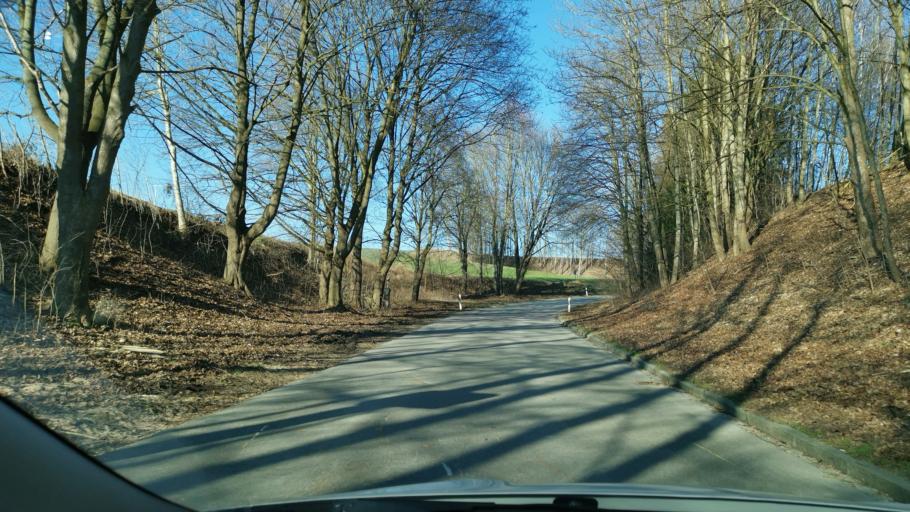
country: DE
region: Bavaria
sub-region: Swabia
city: Aindling
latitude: 48.5190
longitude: 10.9512
